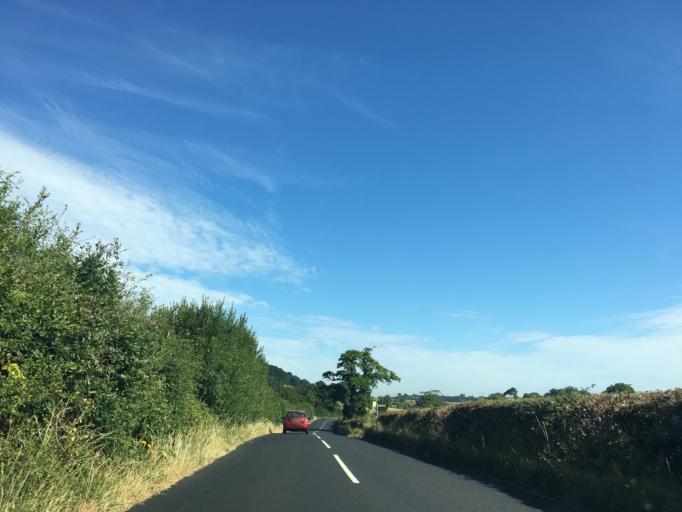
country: GB
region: England
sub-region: Isle of Wight
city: Newport
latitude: 50.6681
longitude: -1.3019
